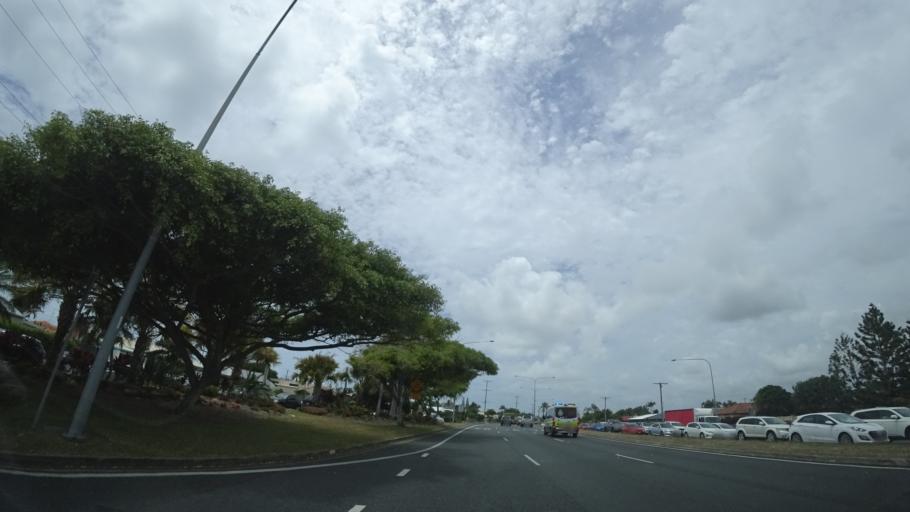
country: AU
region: Queensland
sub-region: Sunshine Coast
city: Mooloolaba
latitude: -26.7055
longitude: 153.1300
